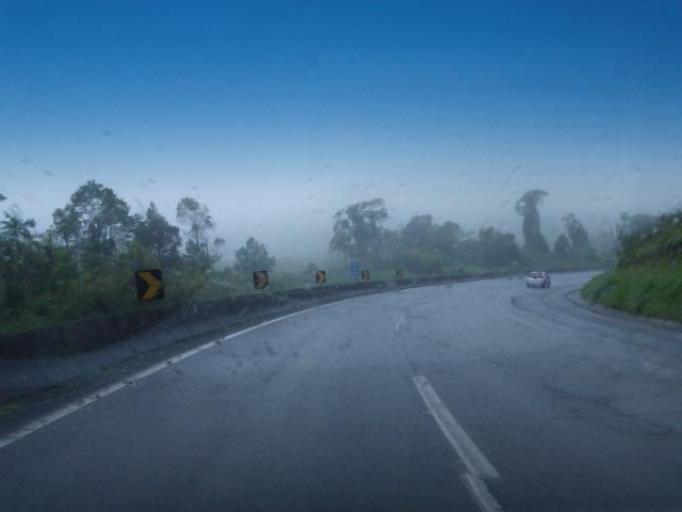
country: BR
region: Parana
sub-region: Antonina
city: Antonina
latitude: -25.1115
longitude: -48.7655
